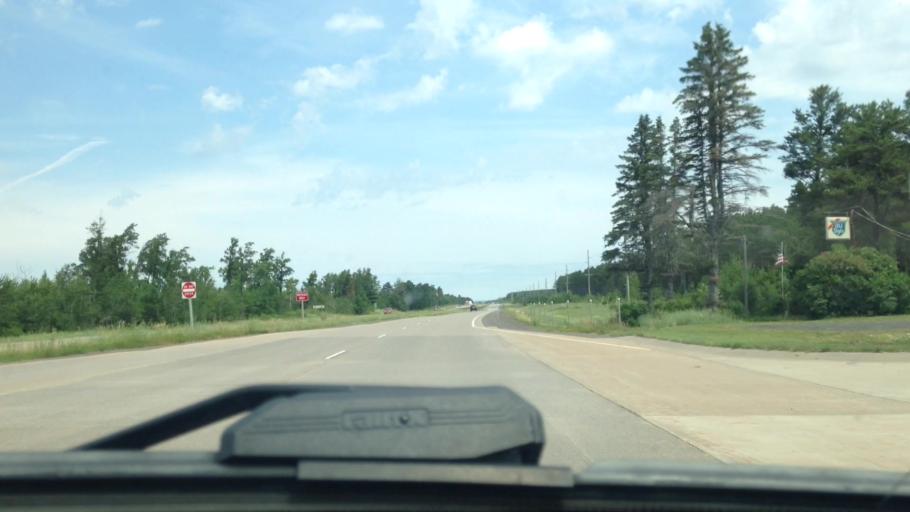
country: US
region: Wisconsin
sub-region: Douglas County
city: Lake Nebagamon
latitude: 46.2879
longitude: -91.8112
